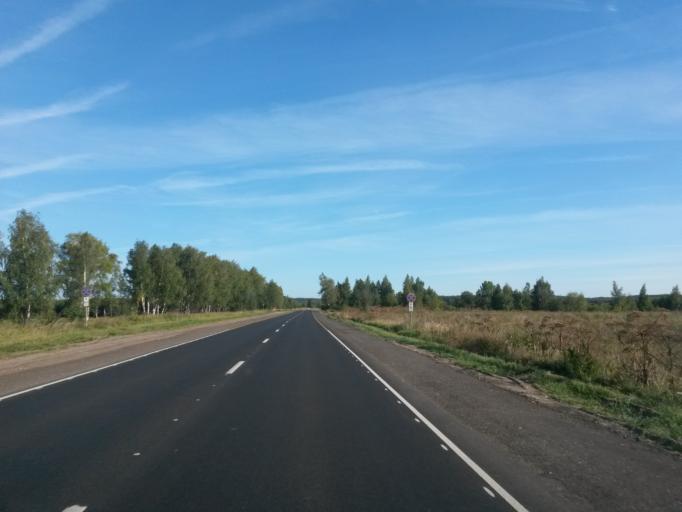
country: RU
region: Jaroslavl
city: Yaroslavl
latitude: 57.5193
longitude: 39.8897
